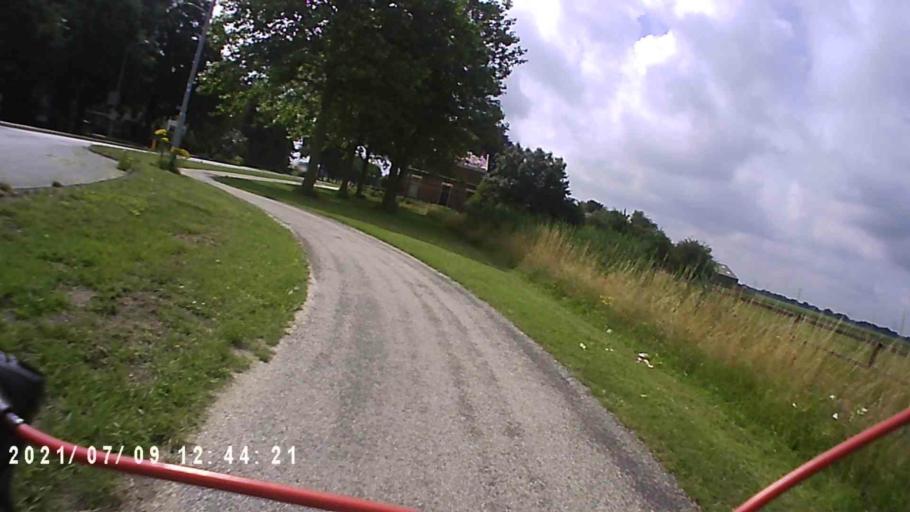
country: NL
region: Groningen
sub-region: Gemeente  Oldambt
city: Winschoten
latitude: 53.1329
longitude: 7.0227
